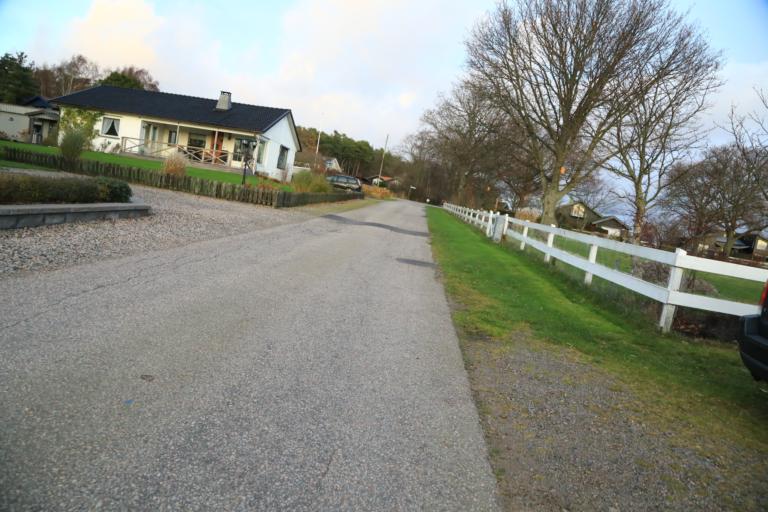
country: SE
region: Halland
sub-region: Varbergs Kommun
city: Varberg
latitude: 57.1424
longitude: 12.2216
